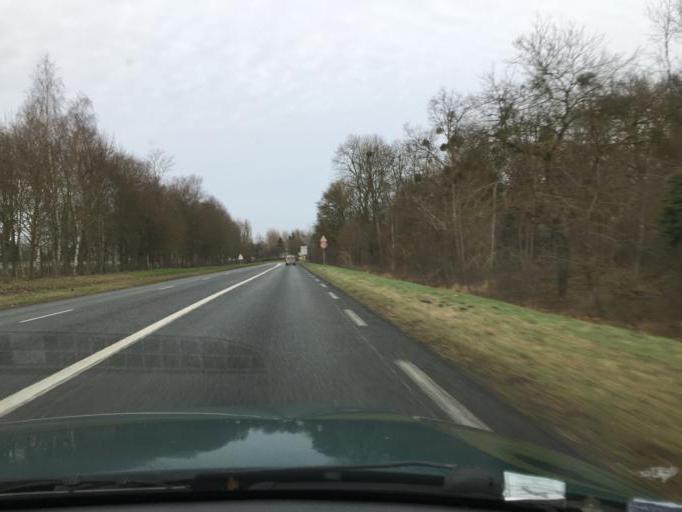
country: FR
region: Picardie
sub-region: Departement de l'Oise
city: Senlis
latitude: 49.1889
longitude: 2.5724
